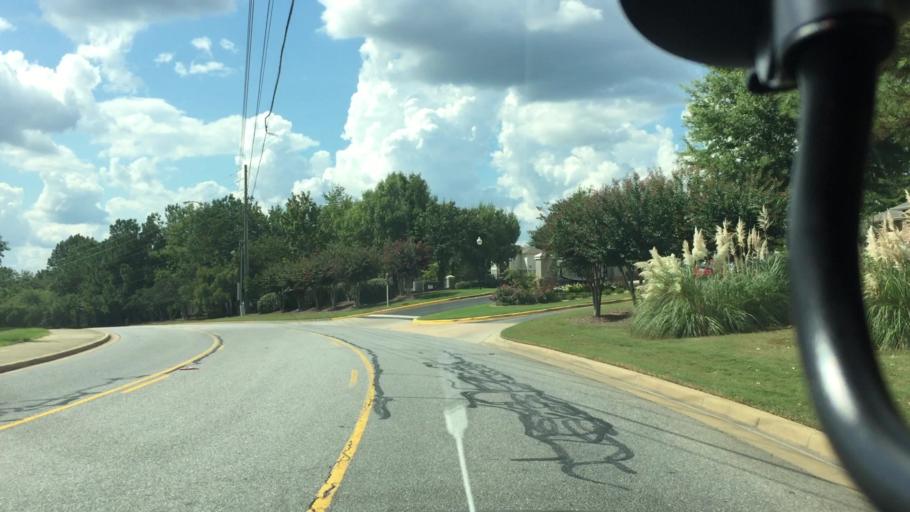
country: US
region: Alabama
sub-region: Lee County
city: Auburn
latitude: 32.5744
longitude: -85.5029
